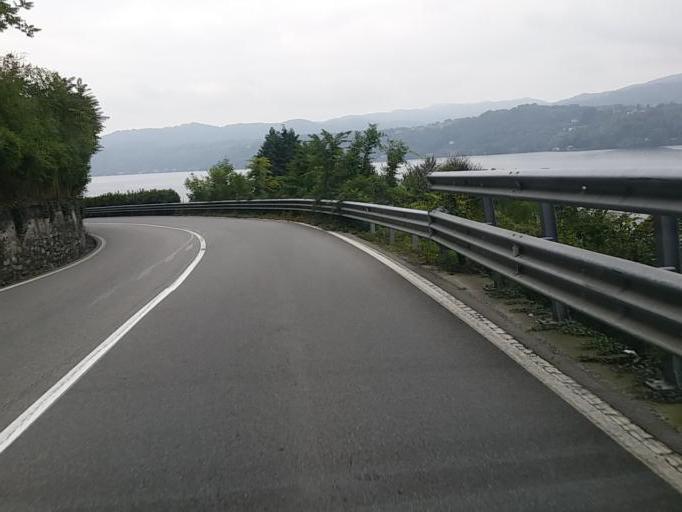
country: IT
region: Piedmont
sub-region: Provincia di Novara
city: Orta San Giulio
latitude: 45.7934
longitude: 8.4176
